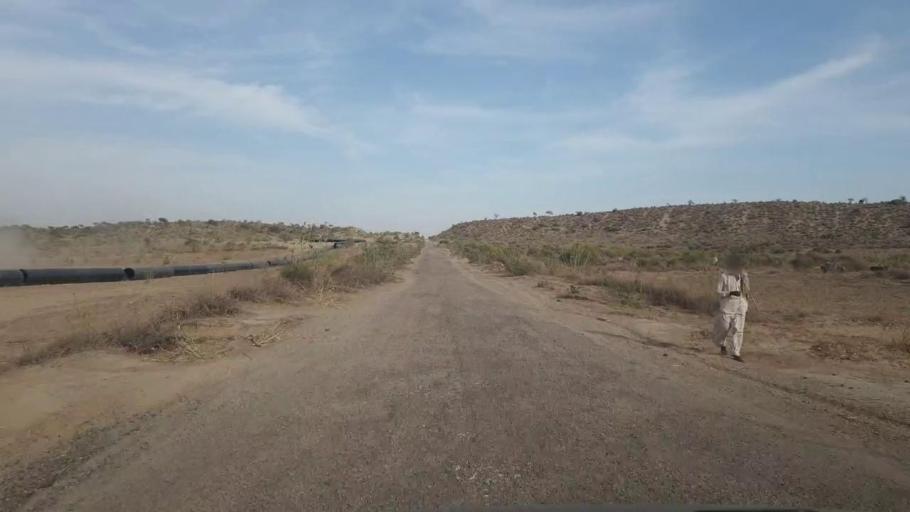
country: PK
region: Sindh
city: Nabisar
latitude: 25.0548
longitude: 69.6793
